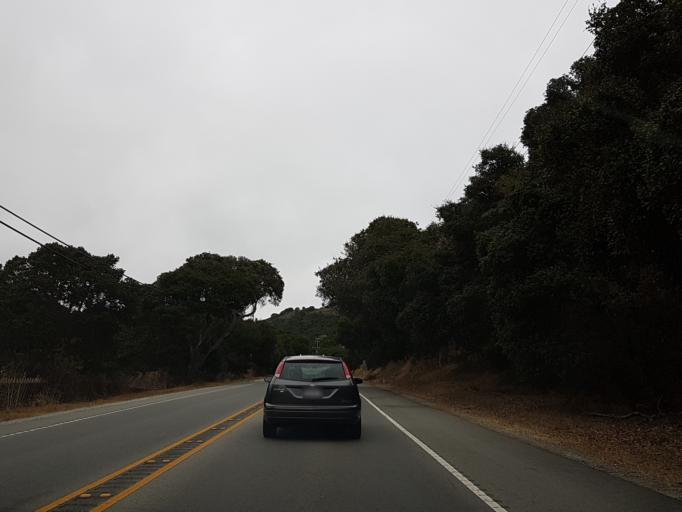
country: US
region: California
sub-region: Monterey County
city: Del Rey Oaks
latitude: 36.5697
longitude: -121.7991
